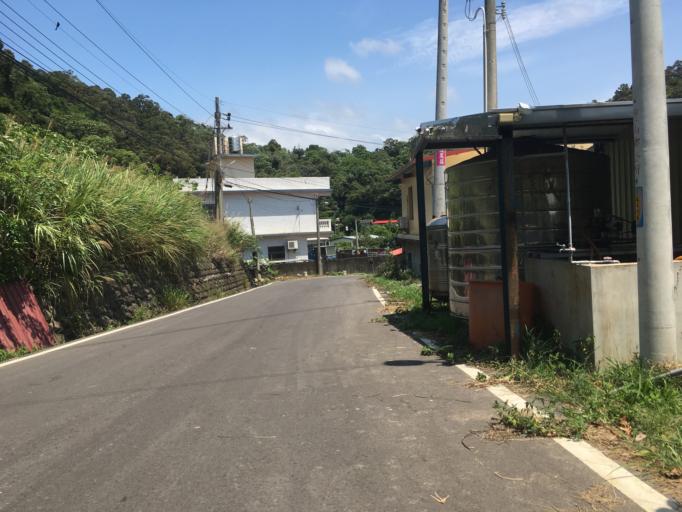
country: TW
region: Taiwan
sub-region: Hsinchu
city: Hsinchu
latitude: 24.7320
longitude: 120.9855
